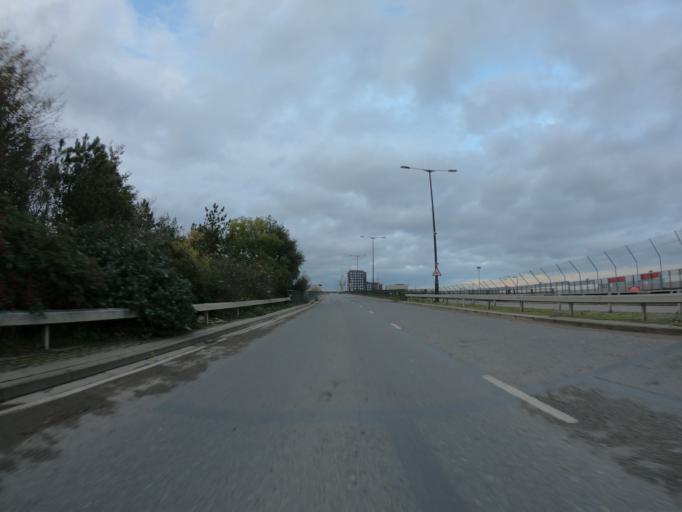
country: GB
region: England
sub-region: Greater London
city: Woolwich
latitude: 51.5051
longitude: 0.0396
